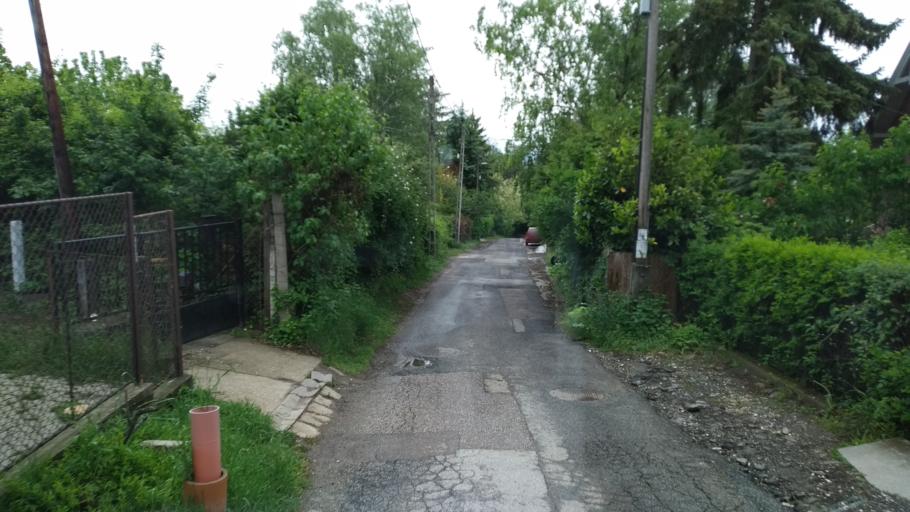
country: HU
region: Pest
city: Szentendre
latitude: 47.6912
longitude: 19.0796
